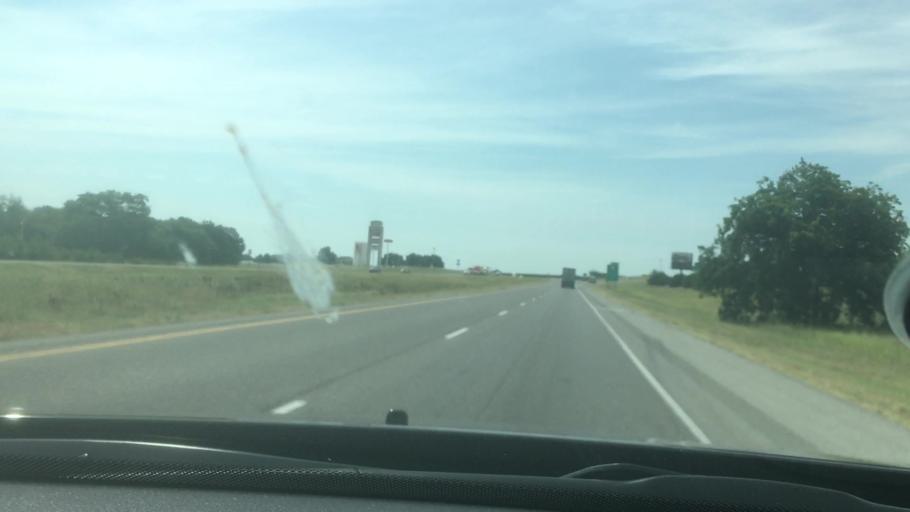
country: US
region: Oklahoma
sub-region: Murray County
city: Davis
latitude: 34.5131
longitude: -97.1790
